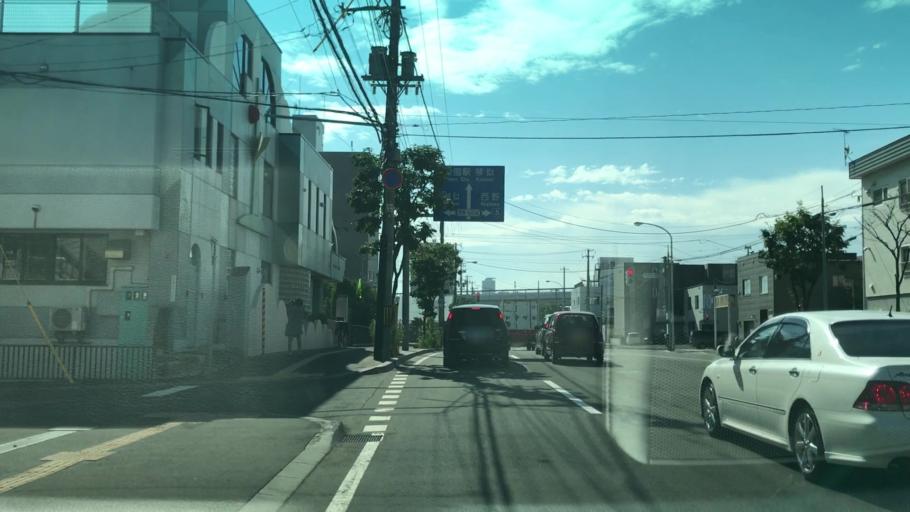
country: JP
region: Hokkaido
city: Sapporo
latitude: 43.0947
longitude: 141.2818
